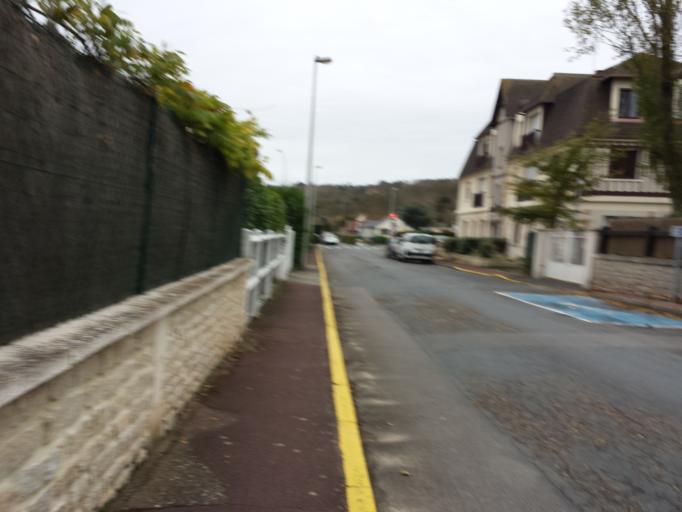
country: FR
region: Lower Normandy
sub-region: Departement du Calvados
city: Deauville
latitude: 49.3495
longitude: 0.0508
